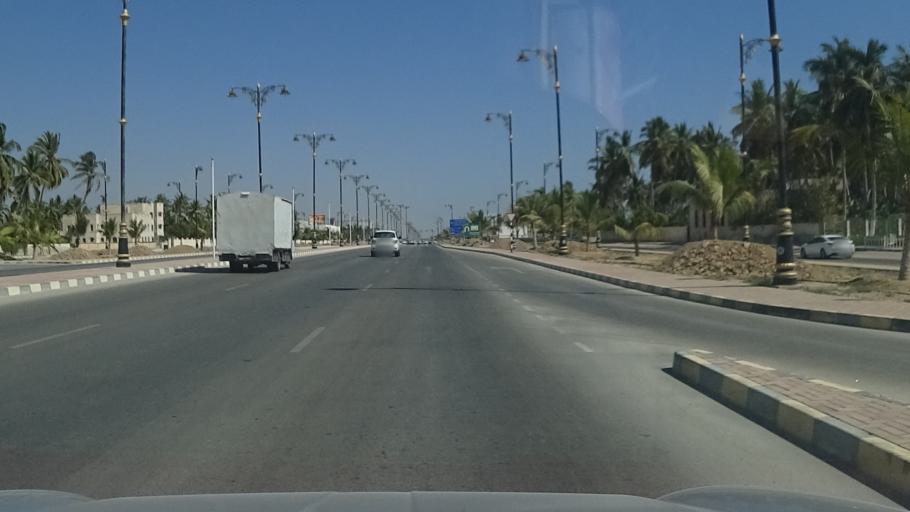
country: OM
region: Zufar
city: Salalah
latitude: 17.0362
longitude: 54.1558
